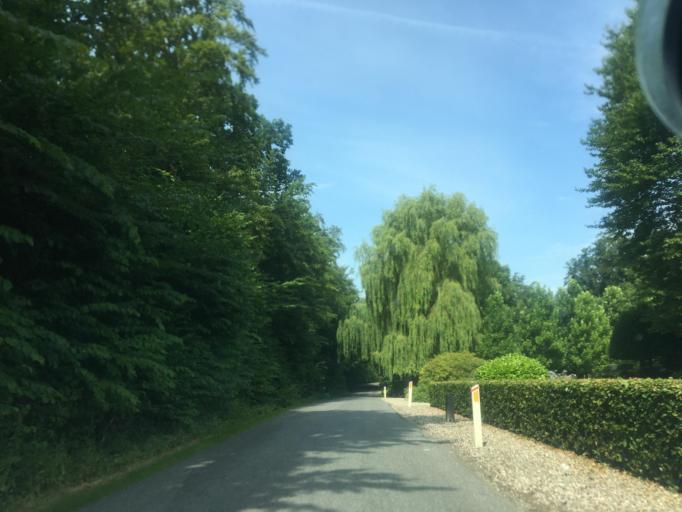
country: DK
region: Zealand
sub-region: Faxe Kommune
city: Fakse
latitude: 55.1941
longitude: 12.0655
